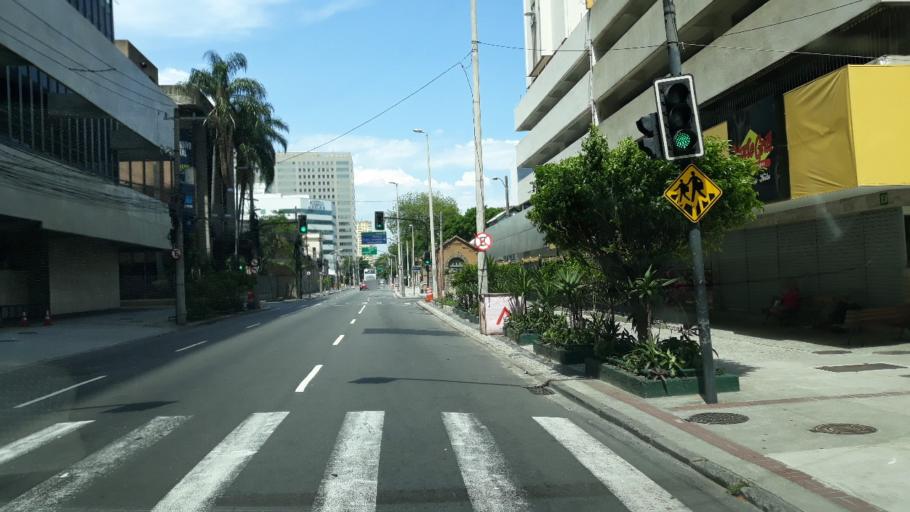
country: BR
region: Rio de Janeiro
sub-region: Rio De Janeiro
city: Rio de Janeiro
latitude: -22.9100
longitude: -43.2029
